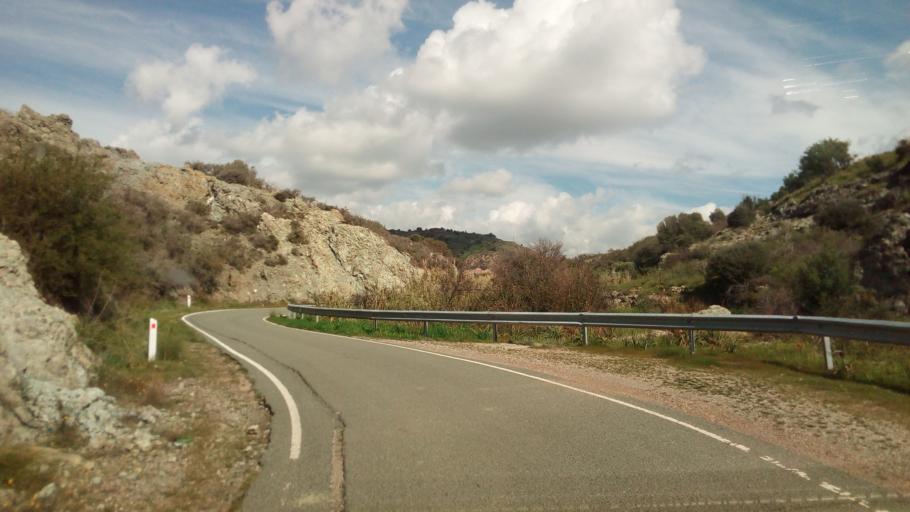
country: CY
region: Pafos
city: Mesogi
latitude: 34.7652
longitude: 32.5544
